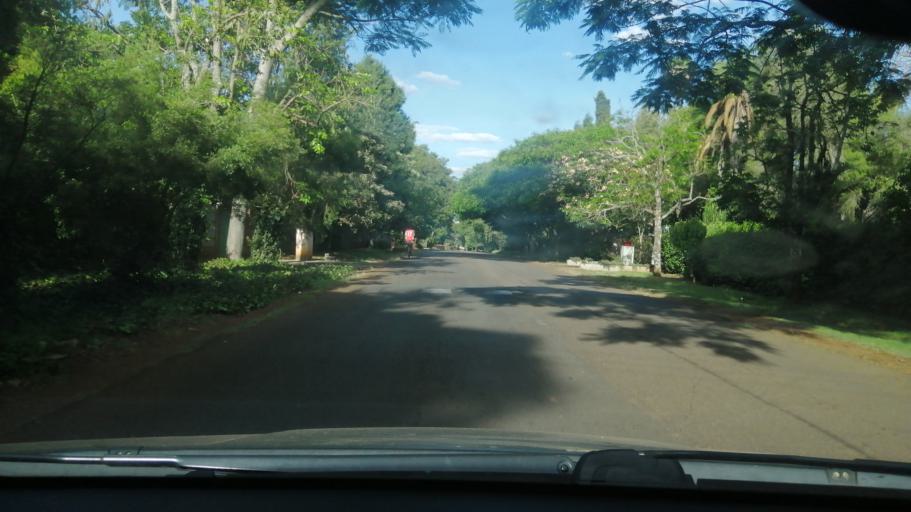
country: ZW
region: Harare
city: Harare
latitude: -17.7656
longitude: 31.0584
